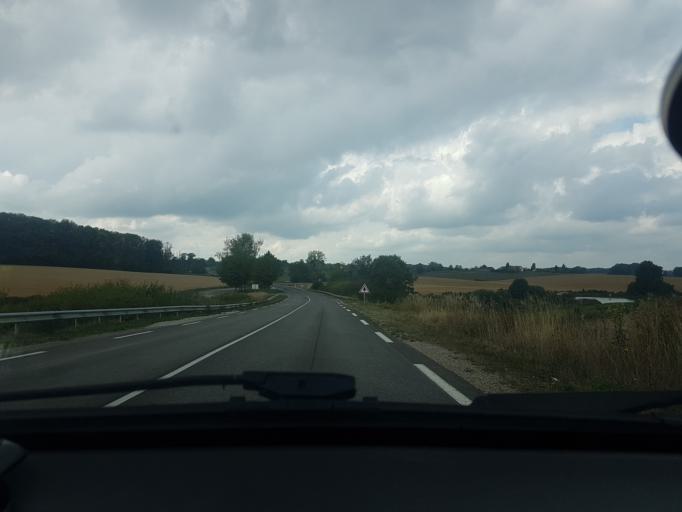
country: FR
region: Franche-Comte
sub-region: Departement de la Haute-Saone
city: Villersexel
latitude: 47.5455
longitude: 6.4737
